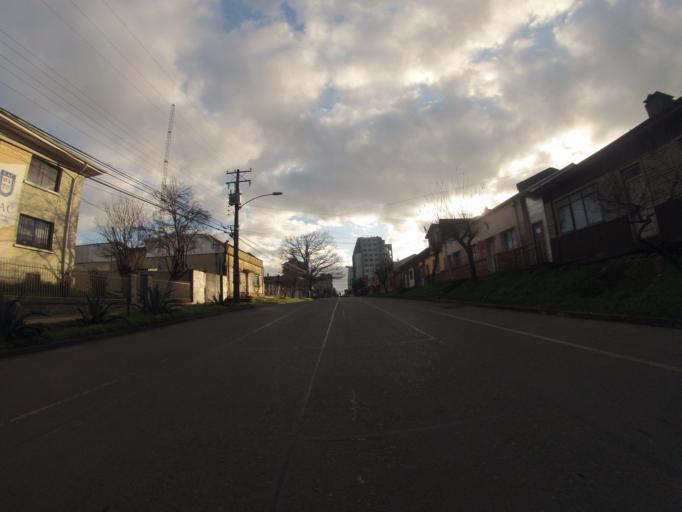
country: CL
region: Araucania
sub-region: Provincia de Cautin
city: Temuco
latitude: -38.7430
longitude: -72.5879
